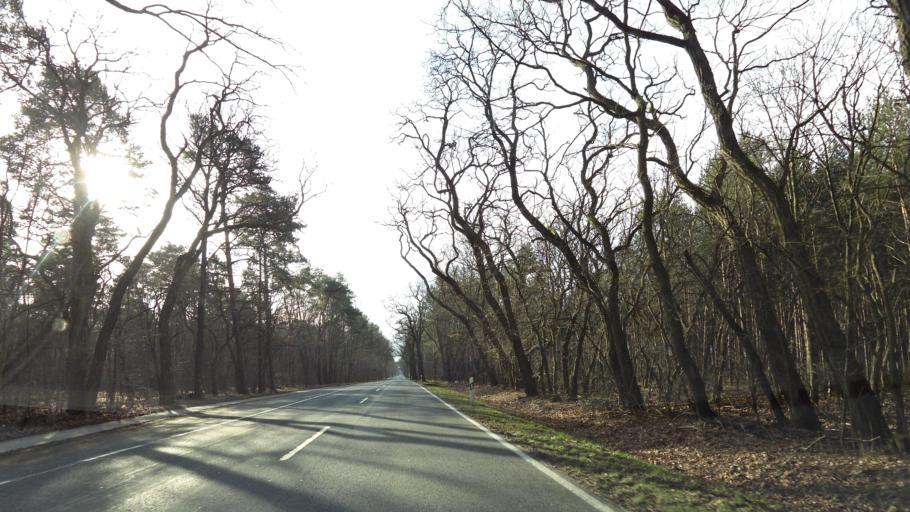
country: DE
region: Brandenburg
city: Michendorf
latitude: 52.3275
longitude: 13.0373
